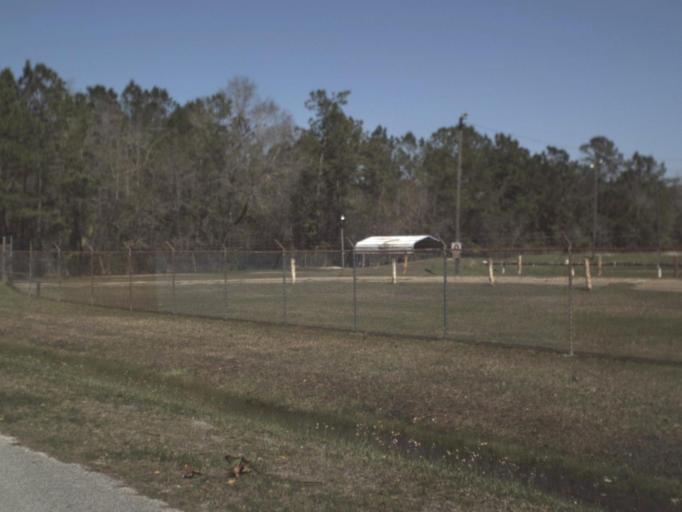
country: US
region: Florida
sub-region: Leon County
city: Woodville
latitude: 30.1665
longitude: -84.2078
